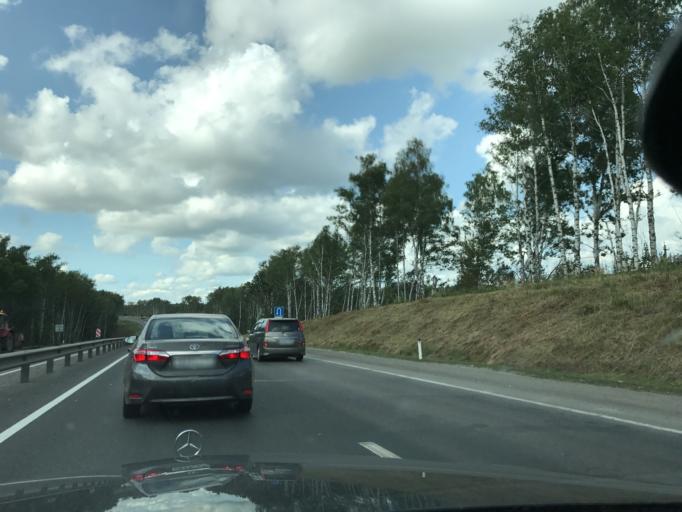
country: RU
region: Vladimir
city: Novovyazniki
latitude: 56.1993
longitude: 42.3621
